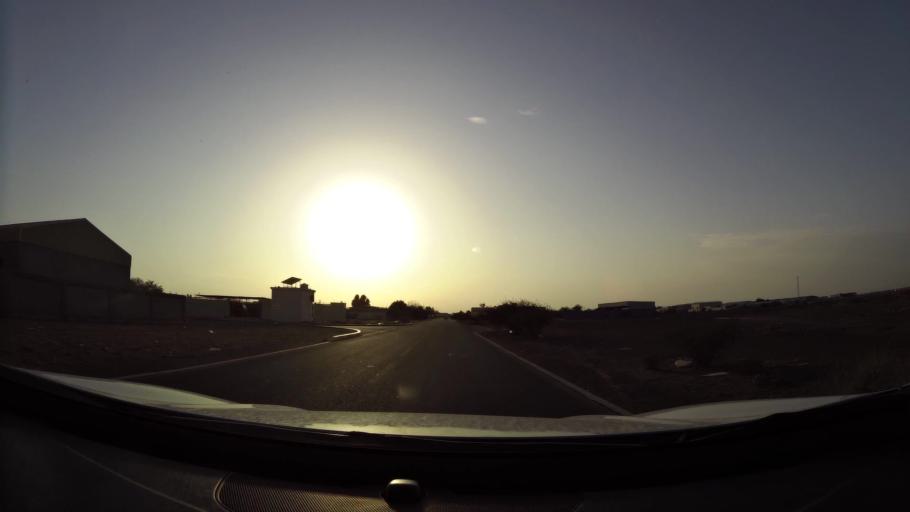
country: AE
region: Abu Dhabi
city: Al Ain
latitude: 24.1557
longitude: 55.8289
